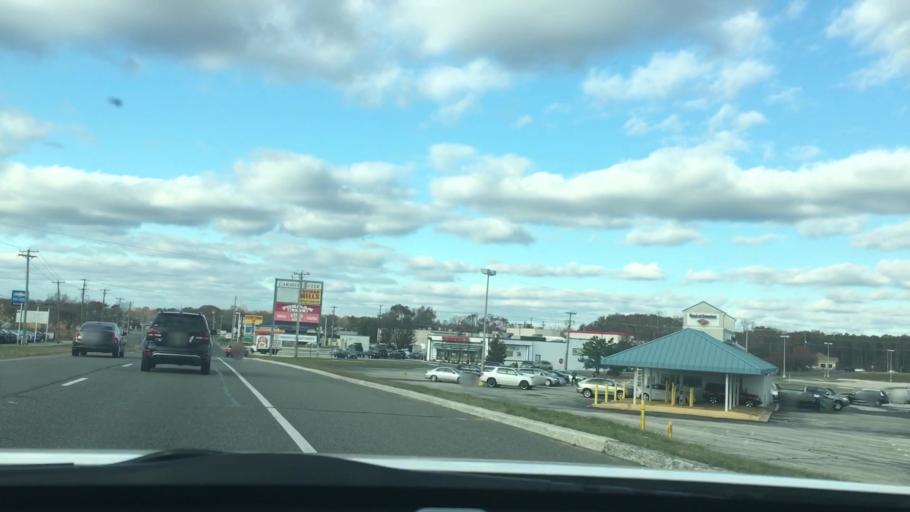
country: US
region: New Jersey
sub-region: Atlantic County
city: Northfield
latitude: 39.4031
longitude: -74.5624
